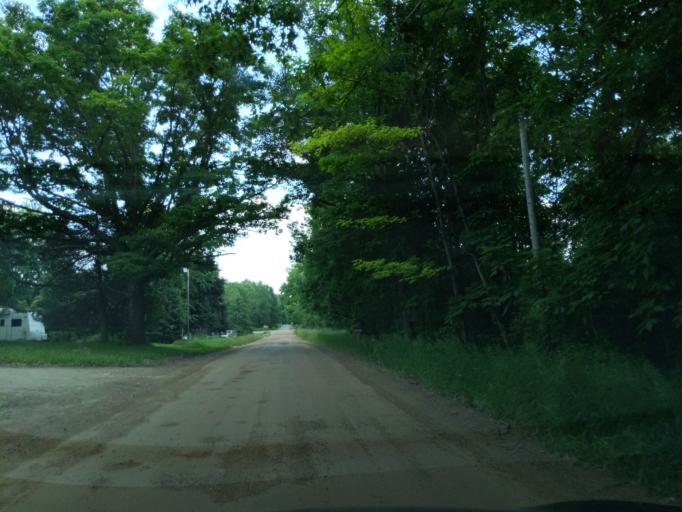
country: US
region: Michigan
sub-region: Shiawassee County
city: Laingsburg
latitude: 42.8204
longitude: -84.3741
